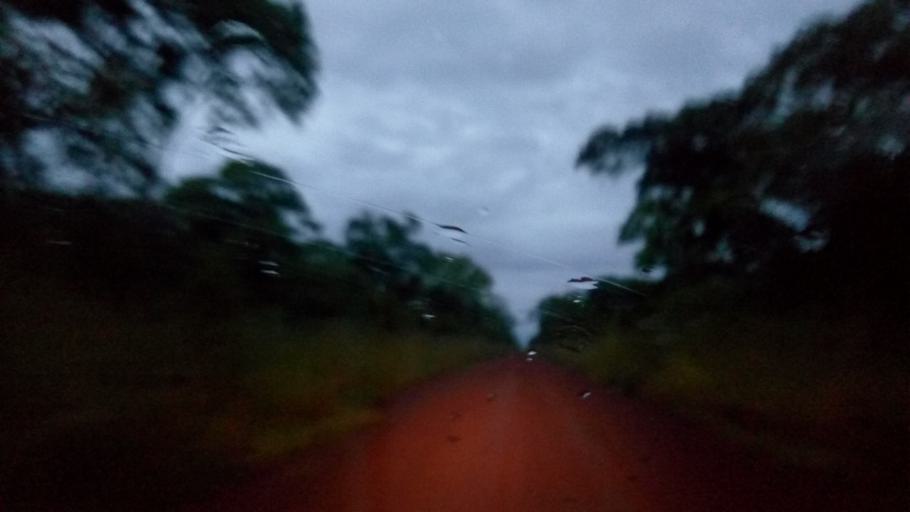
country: ZM
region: Luapula
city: Nchelenge
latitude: -9.7914
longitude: 28.1566
